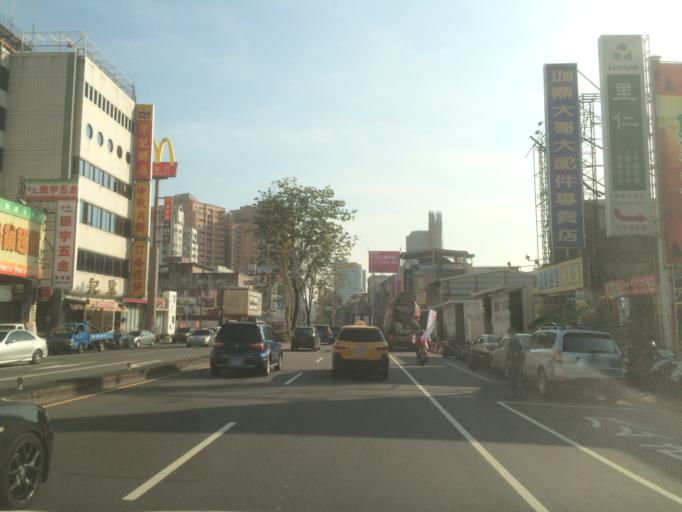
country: TW
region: Taiwan
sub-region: Taichung City
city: Taichung
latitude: 24.1715
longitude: 120.6718
